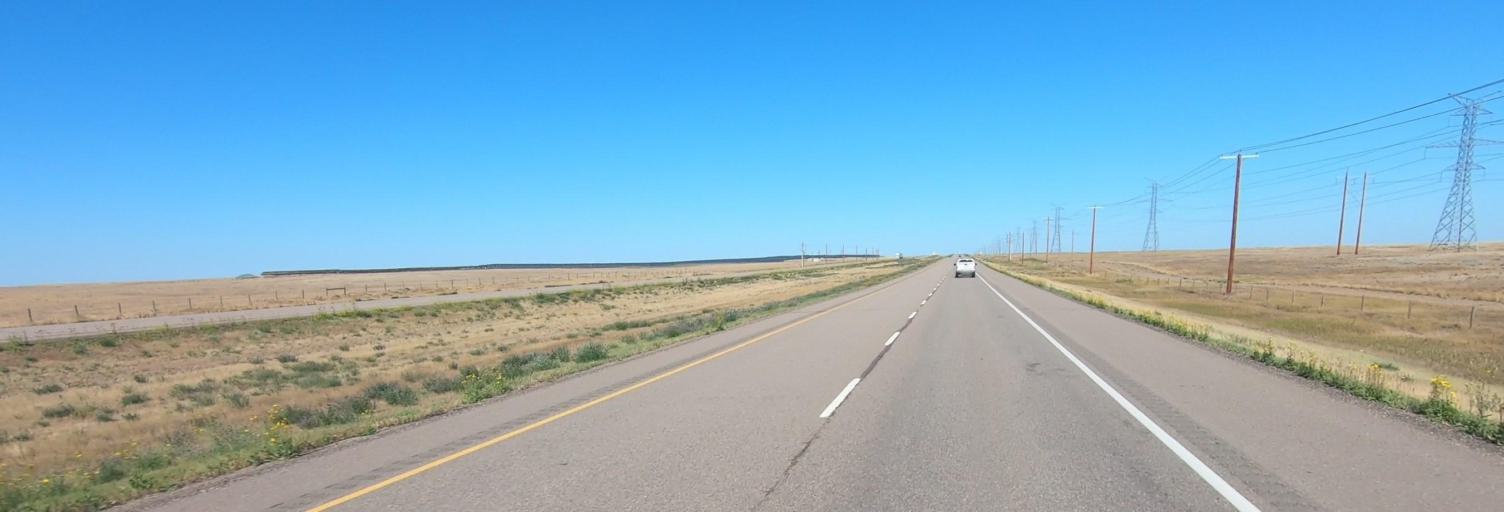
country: CA
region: Alberta
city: Bow Island
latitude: 50.2669
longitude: -111.2580
